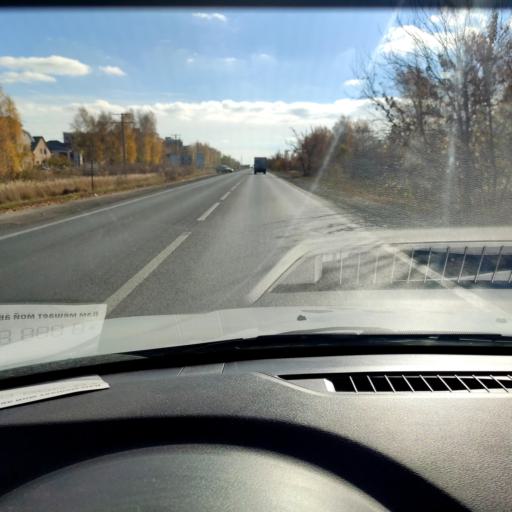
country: RU
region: Samara
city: Tol'yatti
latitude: 53.5536
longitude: 49.3681
